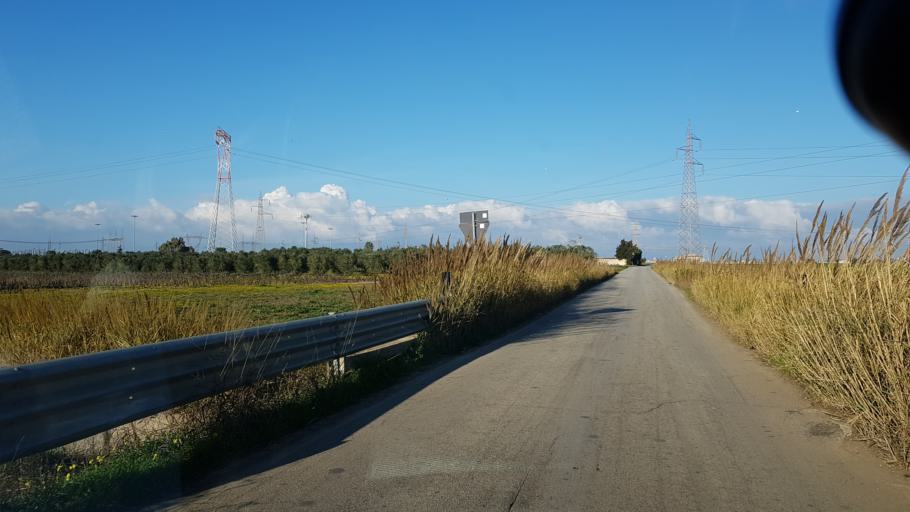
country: IT
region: Apulia
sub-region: Provincia di Brindisi
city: Brindisi
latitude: 40.5958
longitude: 17.9047
